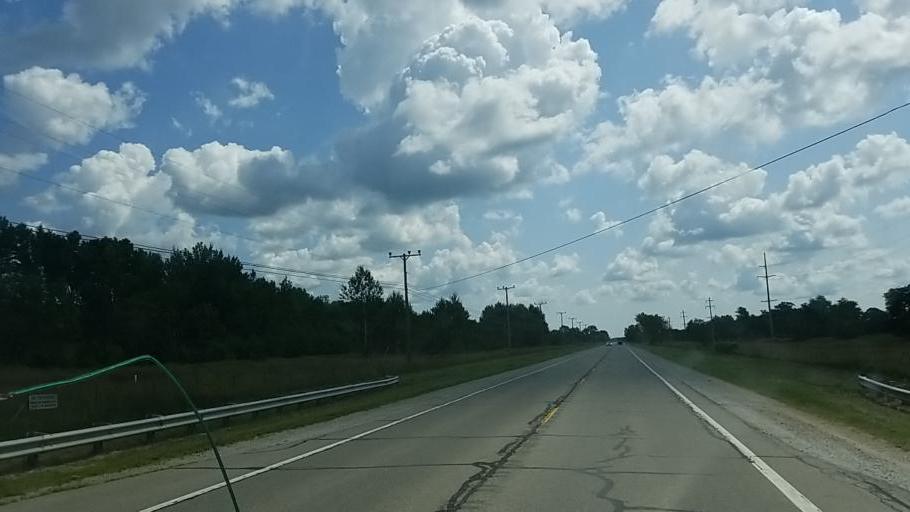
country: US
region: Michigan
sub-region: Muskegon County
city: Wolf Lake
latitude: 43.2353
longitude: -86.0259
